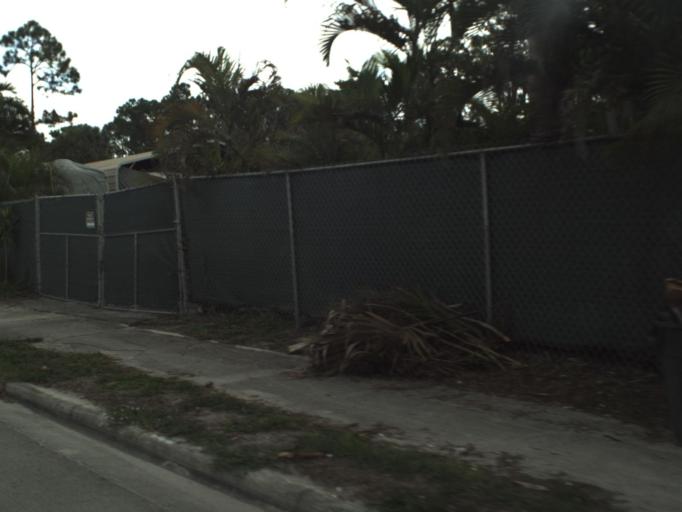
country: US
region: Florida
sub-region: Palm Beach County
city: Lake Belvedere Estates
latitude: 26.6730
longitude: -80.1450
